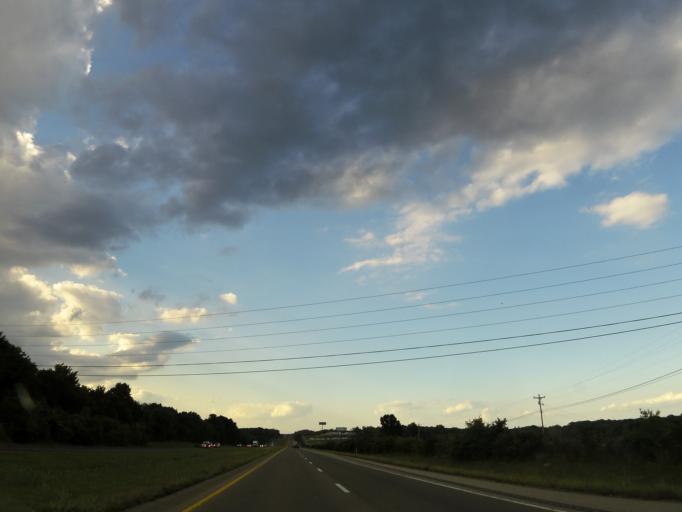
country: US
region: Tennessee
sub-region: Maury County
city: Spring Hill
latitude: 35.6903
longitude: -86.8854
